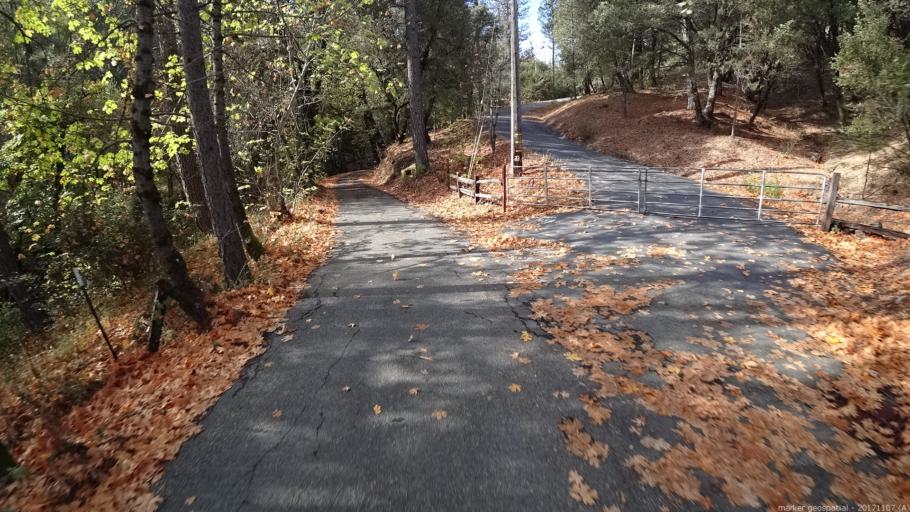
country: US
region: California
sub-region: Shasta County
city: Shasta
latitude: 40.5421
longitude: -122.5821
